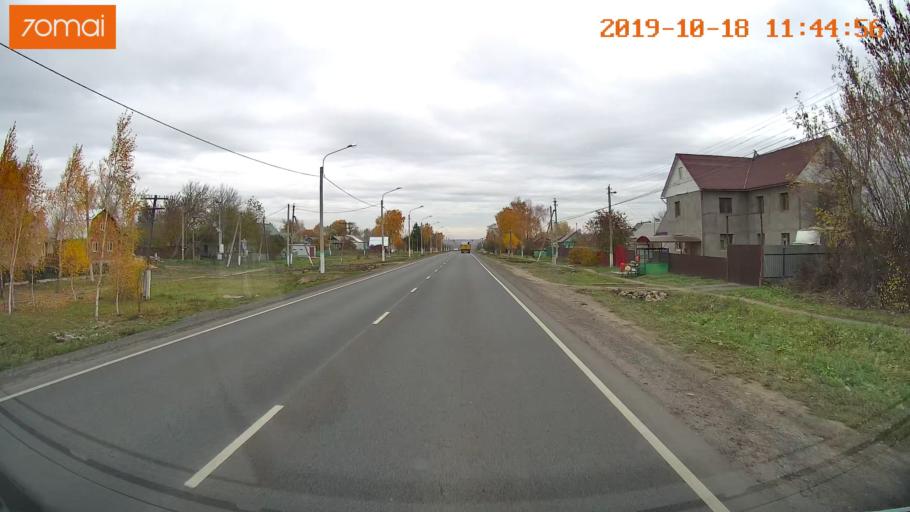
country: RU
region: Rjazan
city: Mikhaylov
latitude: 54.2063
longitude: 38.9640
